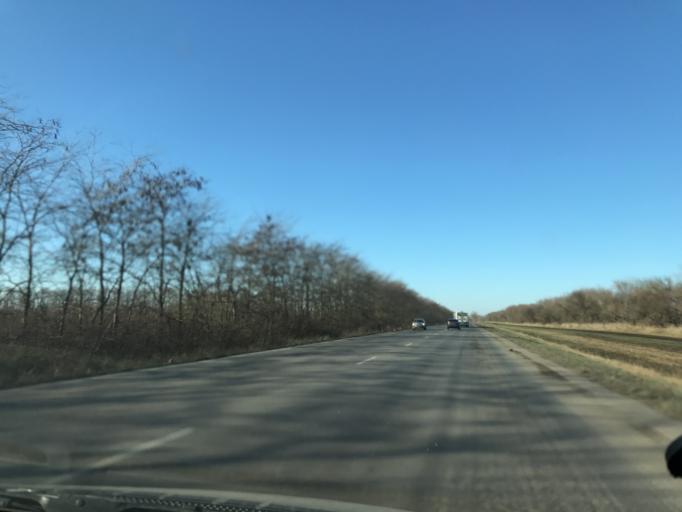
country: RU
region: Rostov
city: Kirovskaya
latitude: 47.0033
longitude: 39.9700
